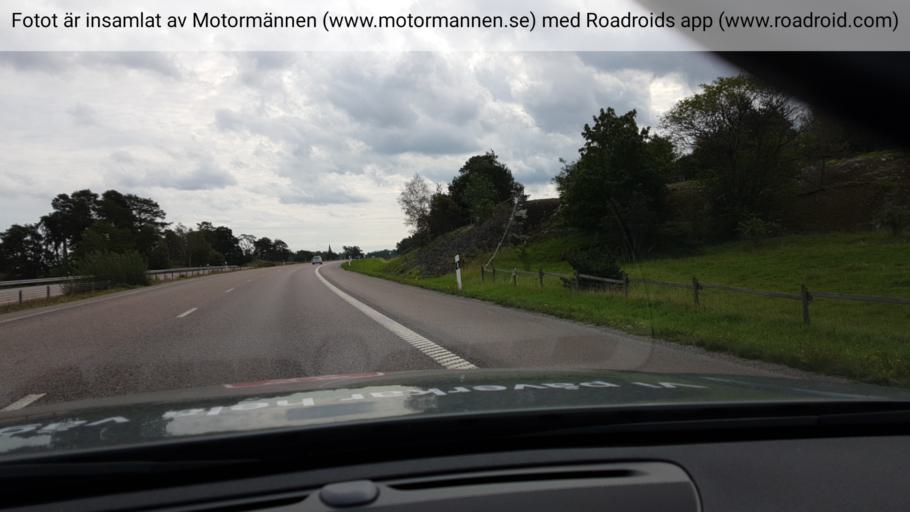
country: SE
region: Uppsala
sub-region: Uppsala Kommun
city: Saevja
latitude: 59.8415
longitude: 17.7181
